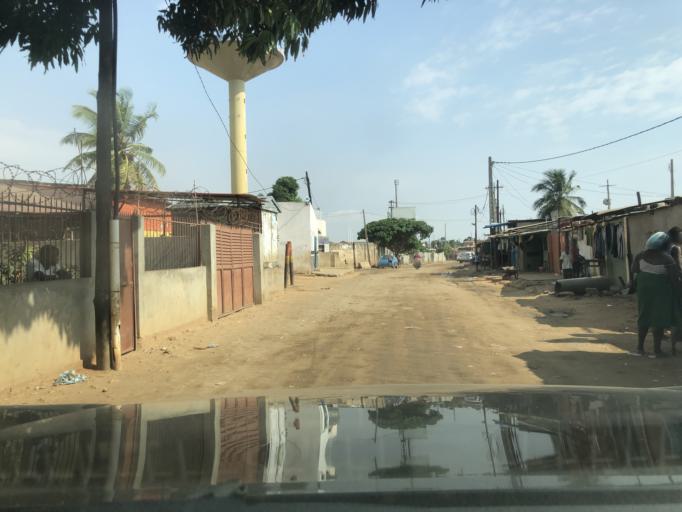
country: AO
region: Luanda
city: Luanda
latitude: -8.8538
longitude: 13.2545
